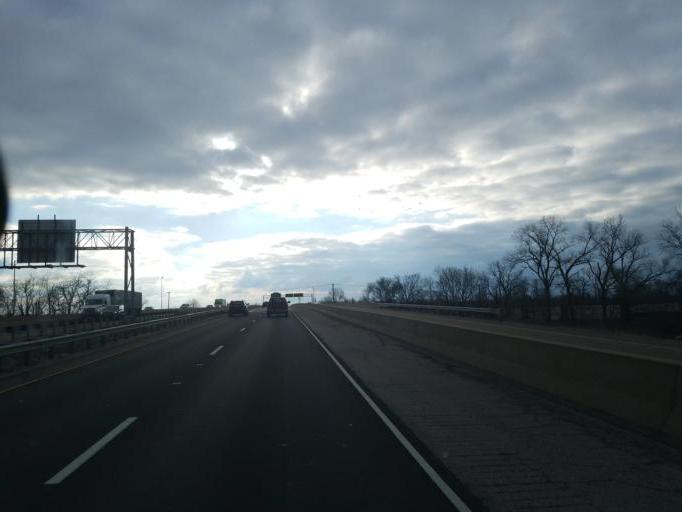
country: US
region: Illinois
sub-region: Madison County
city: Mitchell
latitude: 38.7603
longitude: -90.0967
